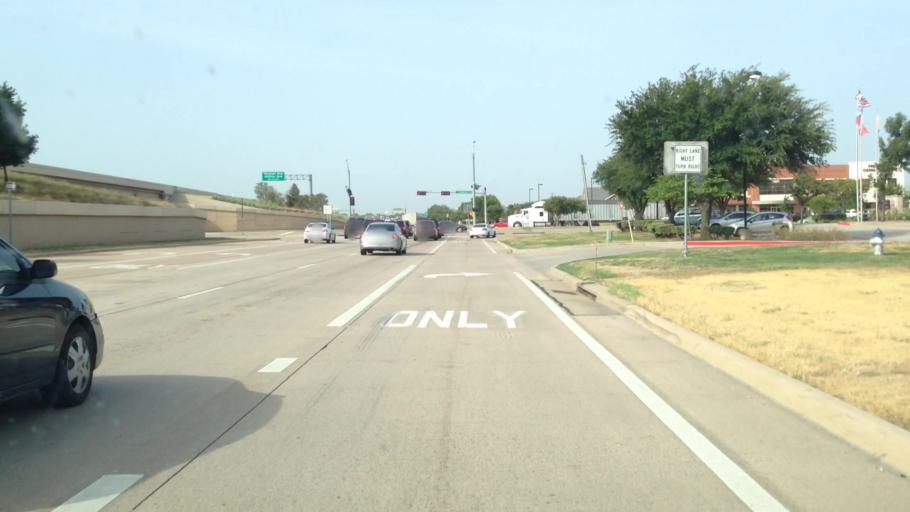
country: US
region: Texas
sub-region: Denton County
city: Lewisville
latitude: 33.0236
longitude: -96.9343
